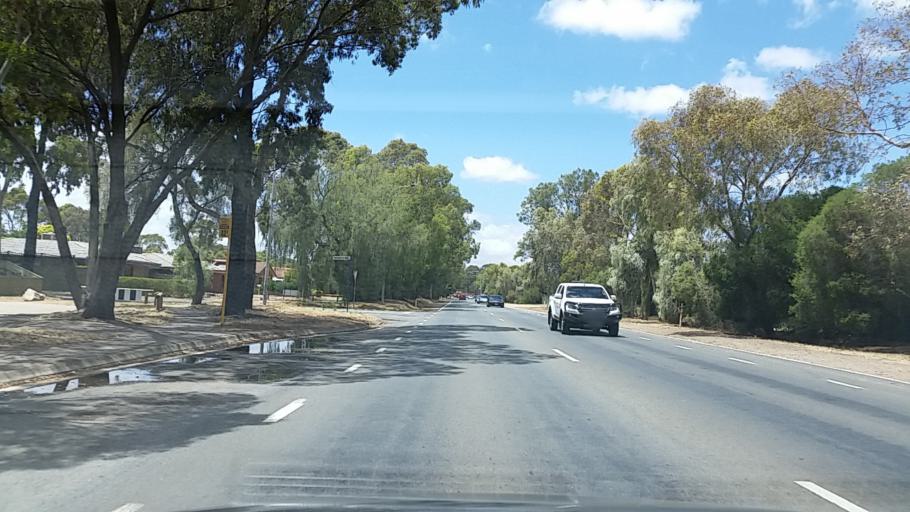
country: AU
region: South Australia
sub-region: Salisbury
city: Salisbury
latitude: -34.7646
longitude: 138.6024
